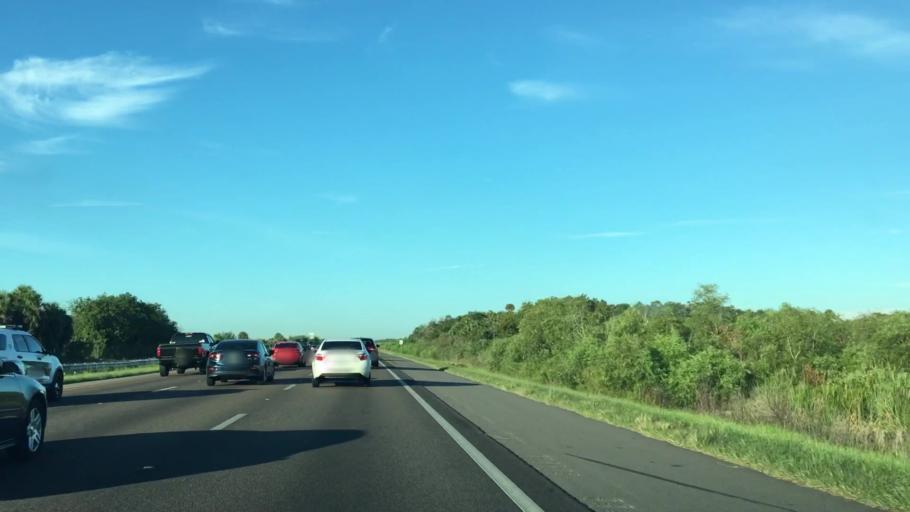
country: US
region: Florida
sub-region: Volusia County
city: DeBary
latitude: 28.8652
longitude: -81.2884
